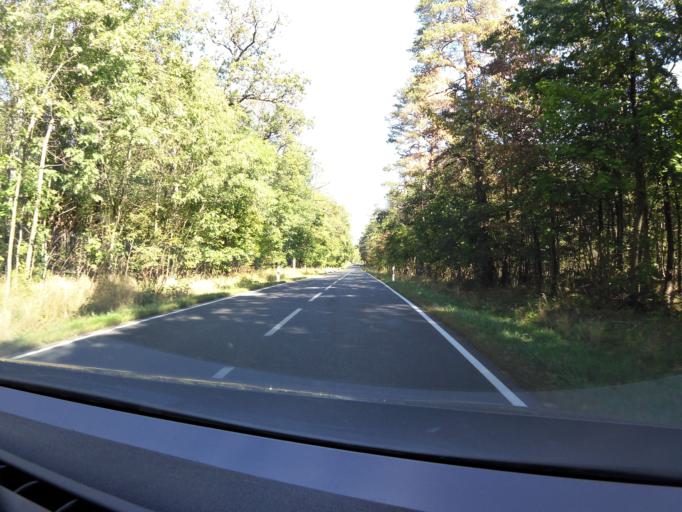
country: DE
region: Saxony-Anhalt
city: Gernrode
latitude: 51.7130
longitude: 11.1364
